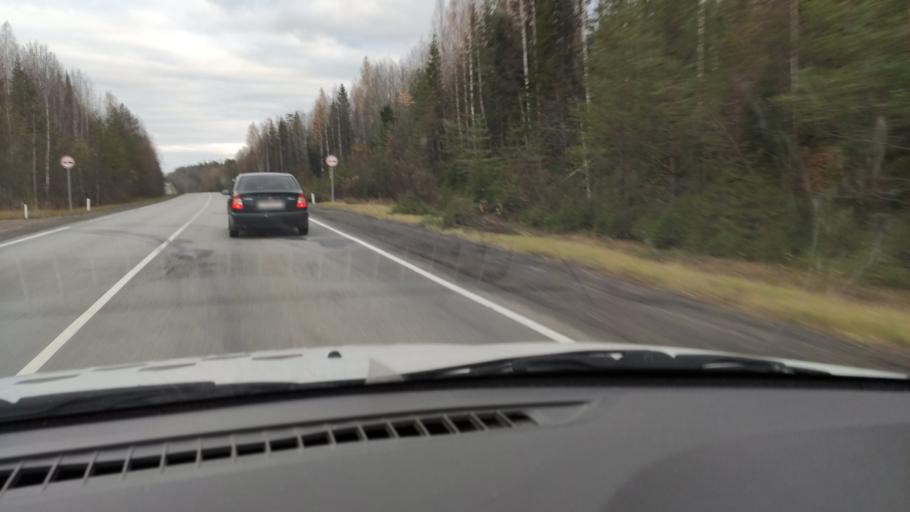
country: RU
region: Kirov
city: Chernaya Kholunitsa
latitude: 58.8659
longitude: 51.5743
